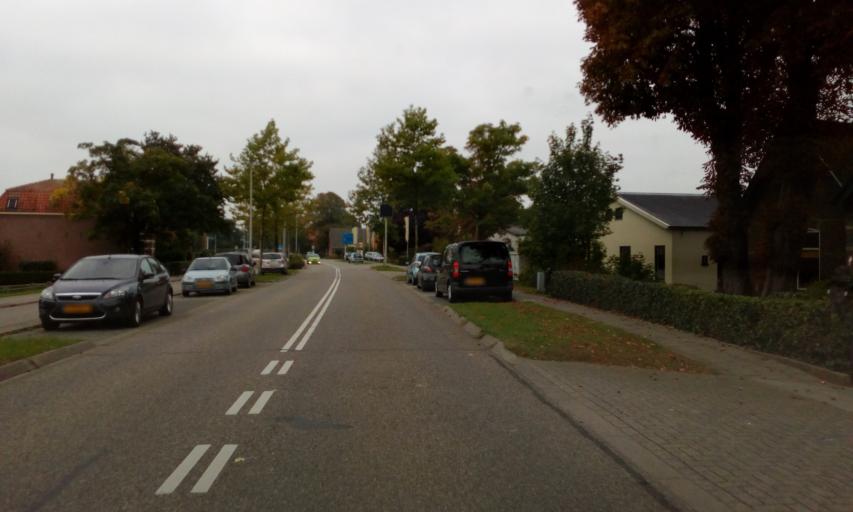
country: NL
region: South Holland
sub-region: Gemeente Alphen aan den Rijn
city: Alphen aan den Rijn
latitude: 52.1311
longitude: 4.5952
